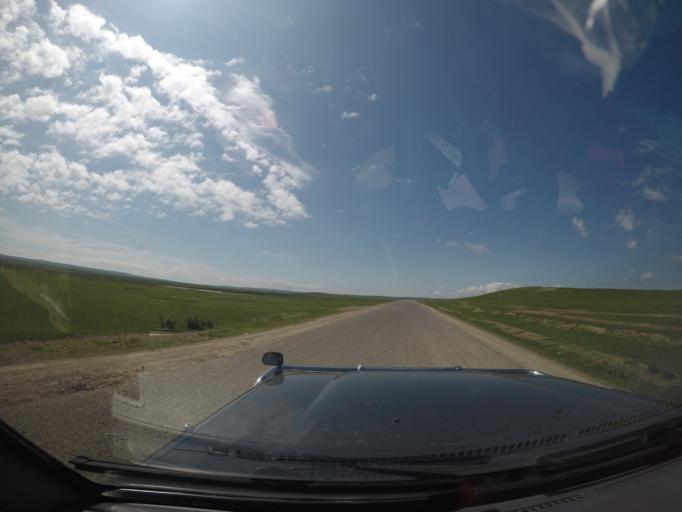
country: MN
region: Hentiy
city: Dundburd
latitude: 47.3302
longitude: 111.4377
